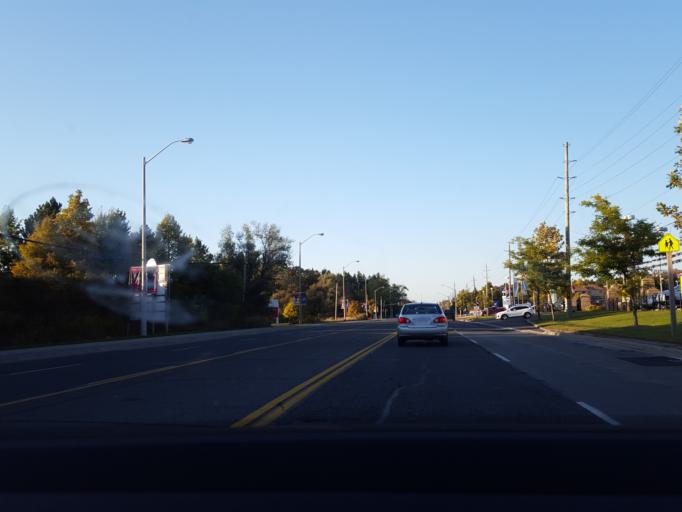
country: CA
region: Ontario
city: Newmarket
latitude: 44.0118
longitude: -79.4704
